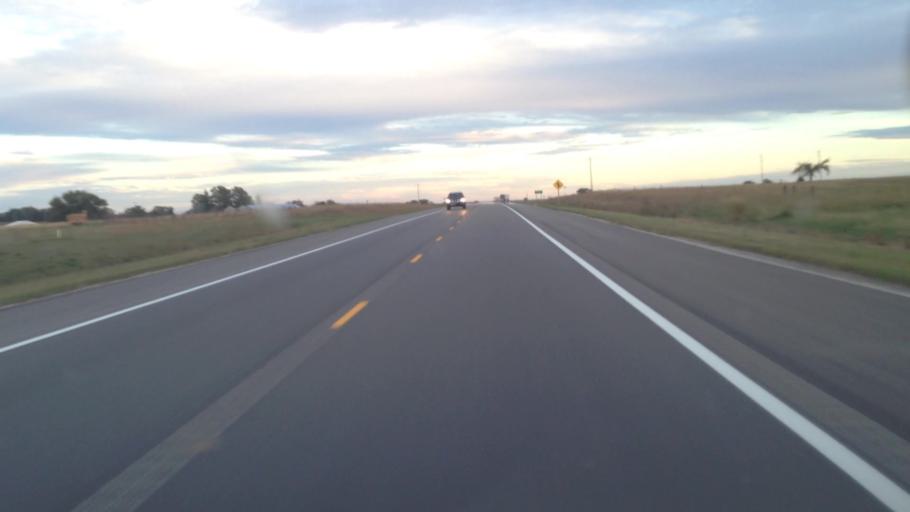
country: US
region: Kansas
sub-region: Franklin County
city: Ottawa
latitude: 38.4651
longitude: -95.2560
